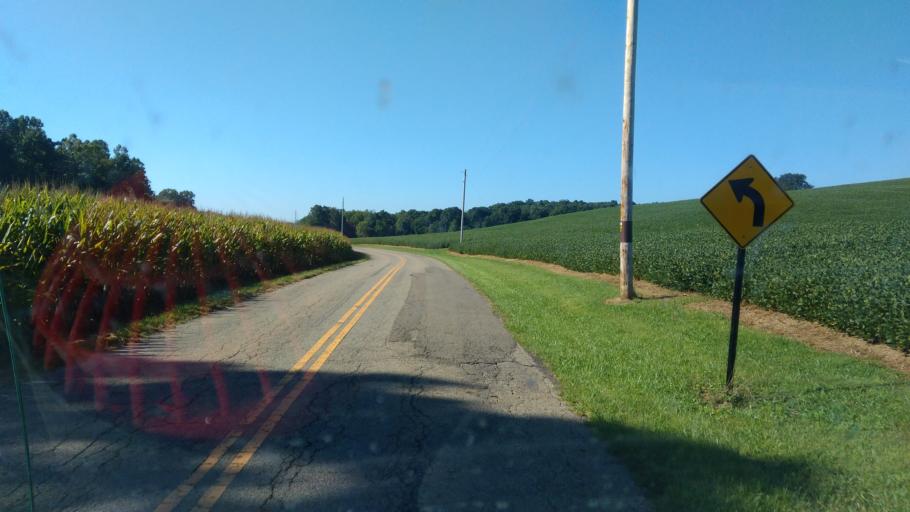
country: US
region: Ohio
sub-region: Knox County
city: Gambier
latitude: 40.4491
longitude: -82.3776
